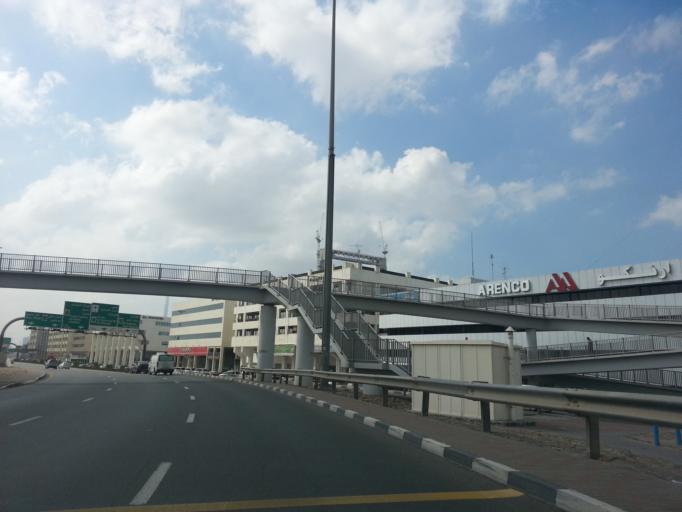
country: AE
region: Ash Shariqah
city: Sharjah
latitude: 25.2394
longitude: 55.3060
